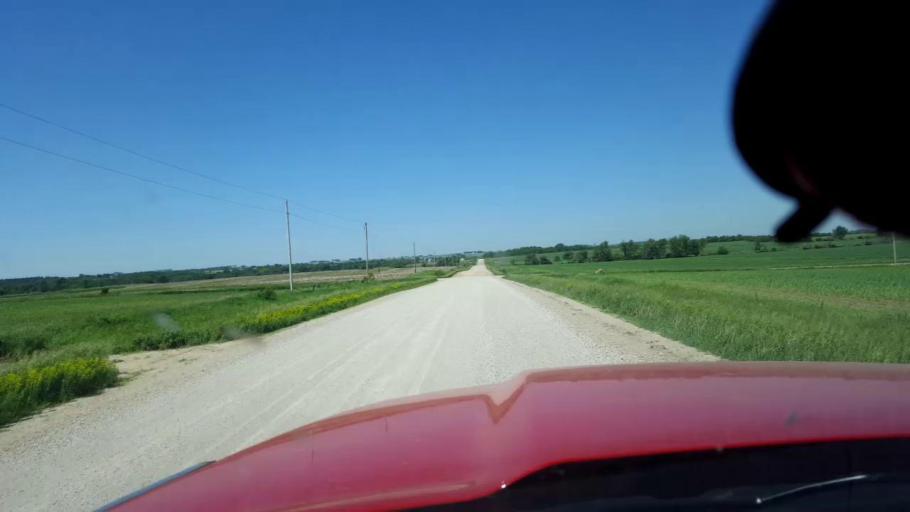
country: US
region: Iowa
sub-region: Chickasaw County
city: New Hampton
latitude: 43.2135
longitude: -92.2579
